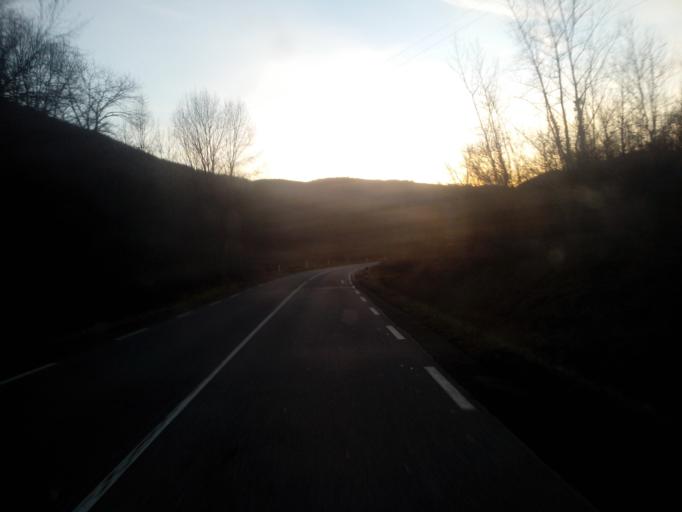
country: FR
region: Midi-Pyrenees
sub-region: Departement de l'Ariege
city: Saint-Paul-de-Jarrat
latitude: 42.9161
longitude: 1.6817
